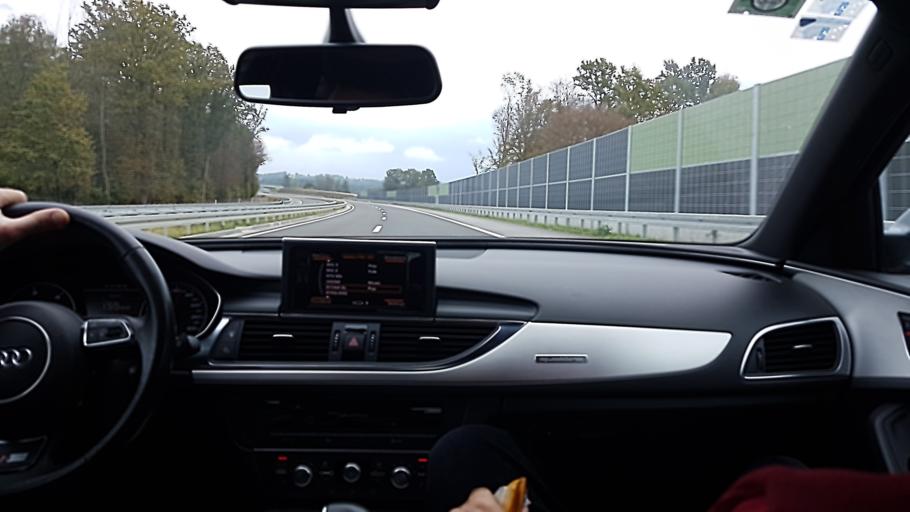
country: BA
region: Republika Srpska
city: Stanari
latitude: 44.8438
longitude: 17.7818
